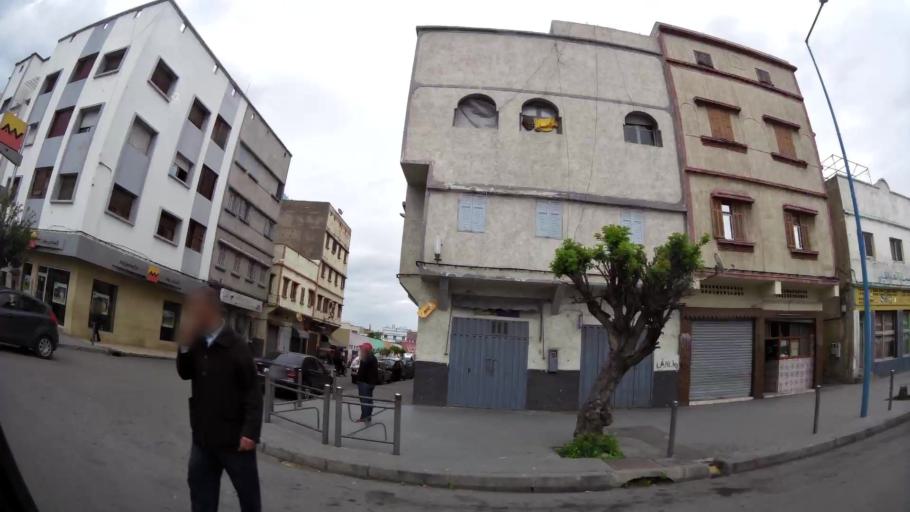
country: MA
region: Grand Casablanca
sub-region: Casablanca
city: Casablanca
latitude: 33.5935
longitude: -7.5694
